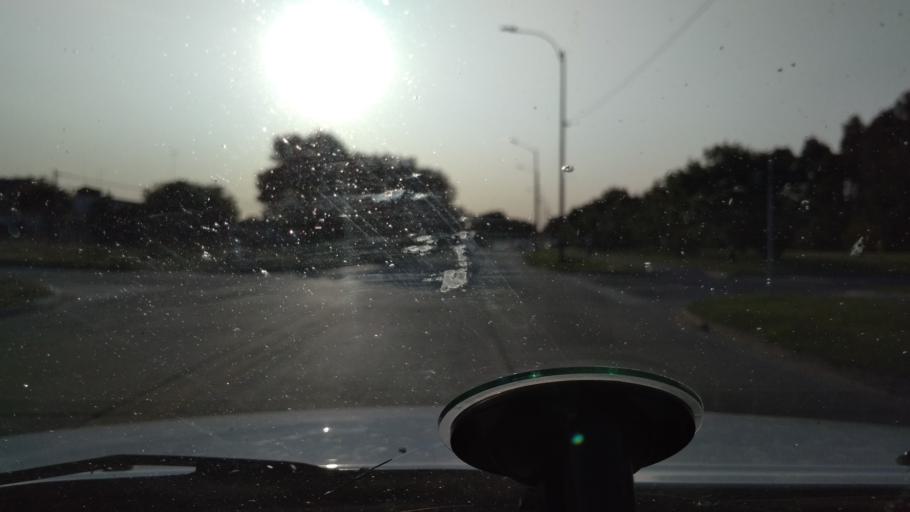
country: UY
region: Canelones
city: Paso de Carrasco
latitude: -34.8703
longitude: -56.0701
